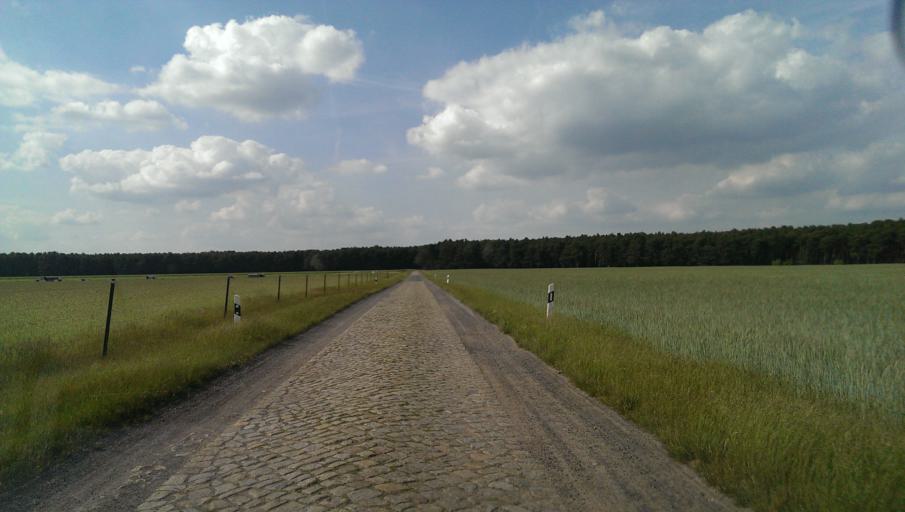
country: DE
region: Brandenburg
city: Linthe
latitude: 52.1547
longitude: 12.7167
